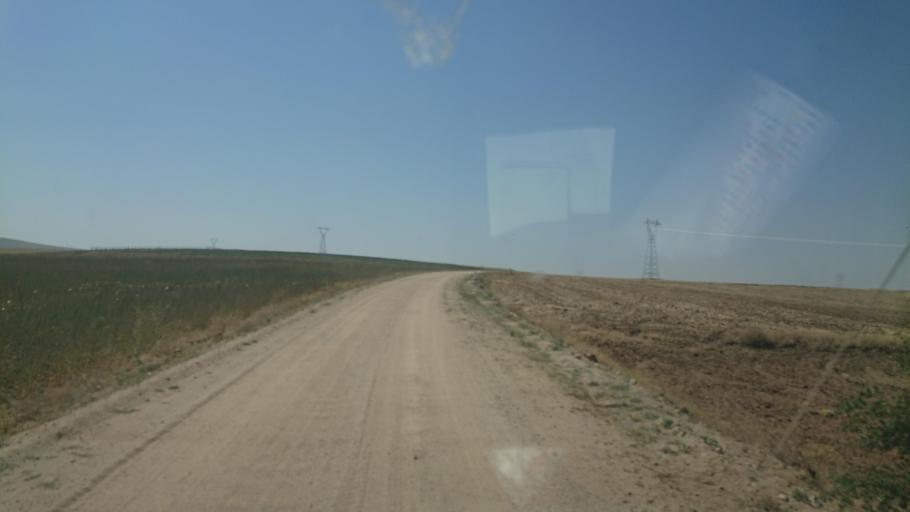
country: TR
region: Aksaray
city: Agacoren
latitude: 38.8043
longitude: 33.9483
